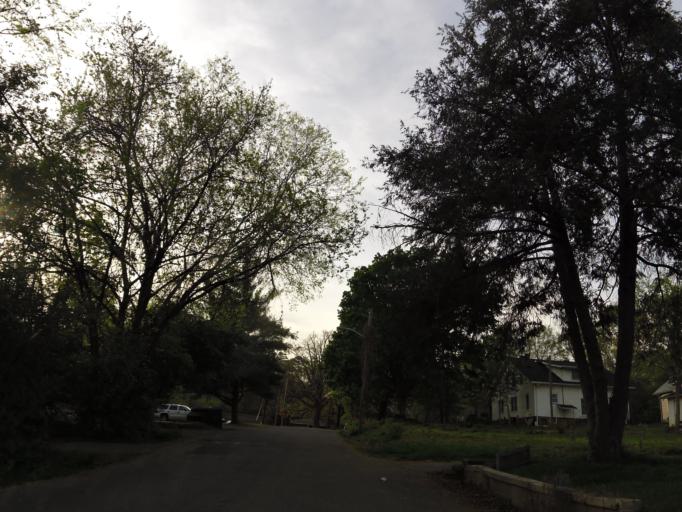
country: US
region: Tennessee
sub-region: Knox County
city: Knoxville
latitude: 36.0405
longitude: -83.9274
